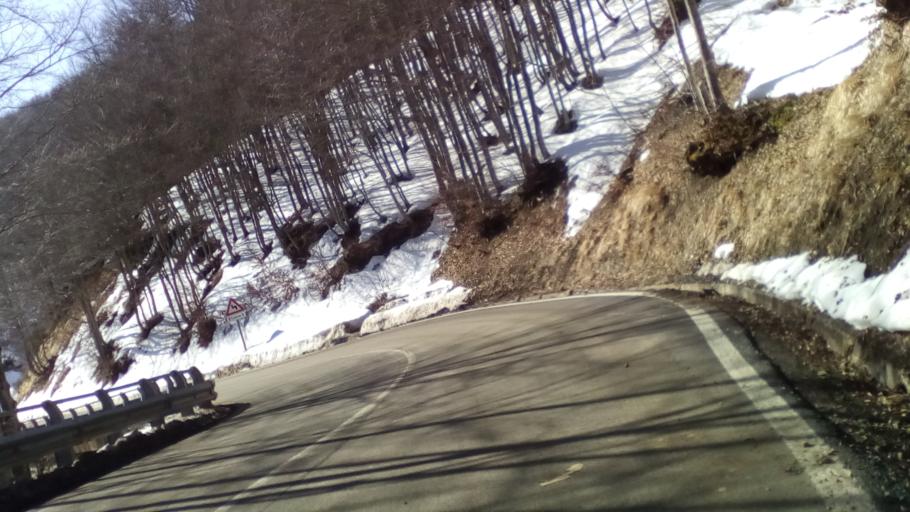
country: IT
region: Tuscany
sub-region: Provincia di Lucca
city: Fosciandora
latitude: 44.2058
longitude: 10.4941
